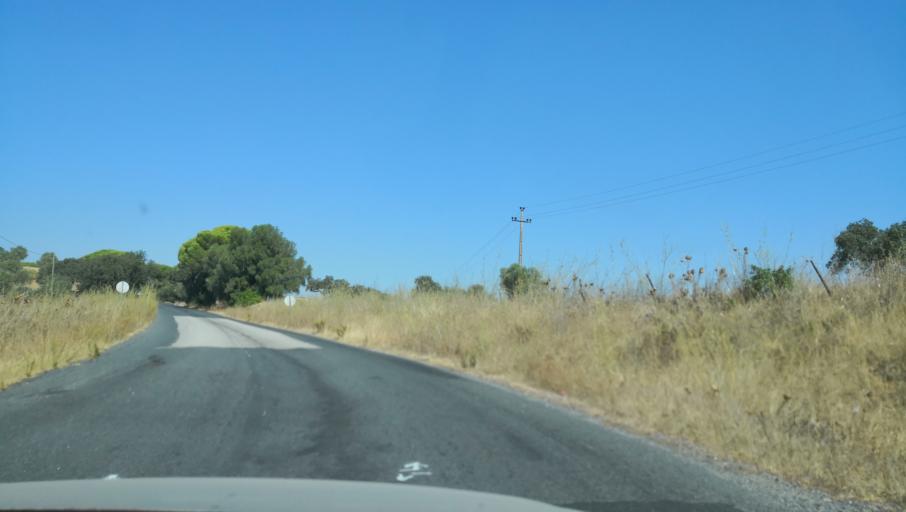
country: PT
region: Setubal
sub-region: Alcacer do Sal
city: Alcacer do Sal
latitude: 38.2912
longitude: -8.4033
